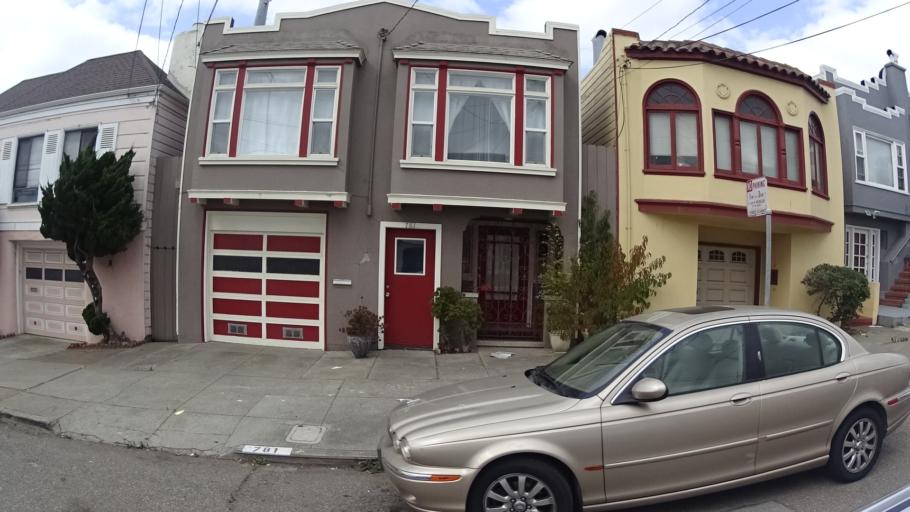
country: US
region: California
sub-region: San Mateo County
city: Daly City
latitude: 37.7739
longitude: -122.5069
